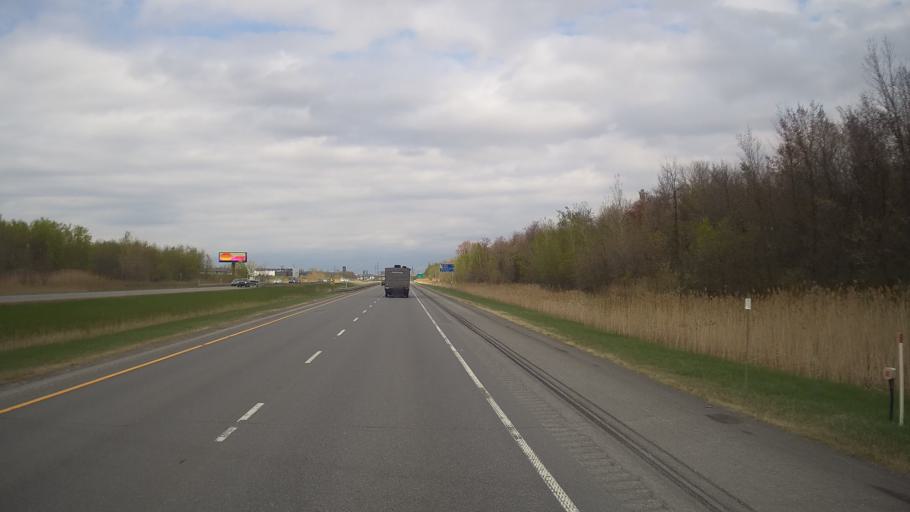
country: CA
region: Quebec
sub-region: Monteregie
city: La Prairie
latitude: 45.3918
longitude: -73.4683
